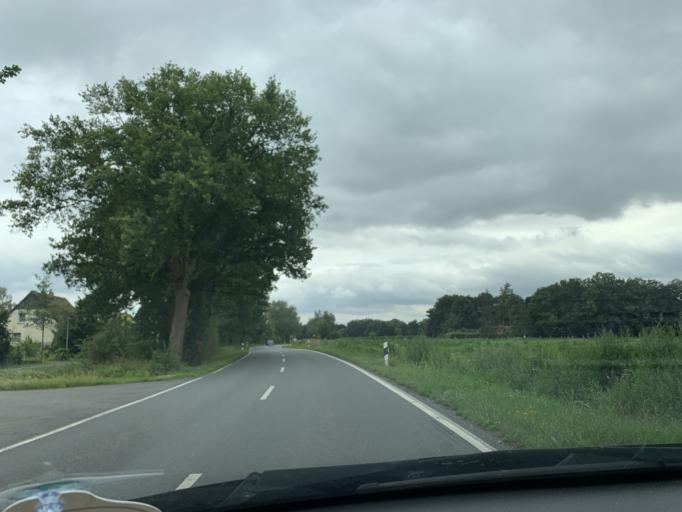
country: DE
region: North Rhine-Westphalia
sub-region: Regierungsbezirk Arnsberg
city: Lippstadt
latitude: 51.6888
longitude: 8.2996
